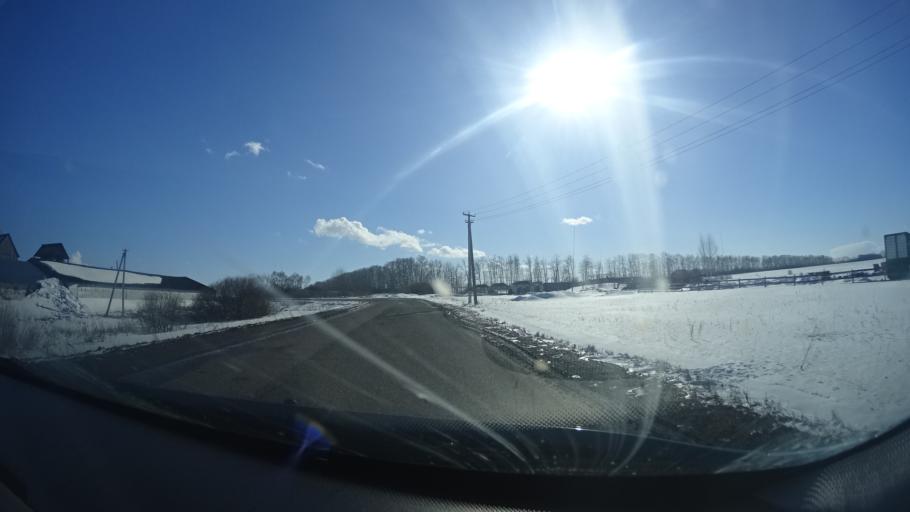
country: RU
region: Bashkortostan
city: Chishmy
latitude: 54.5903
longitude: 55.2575
